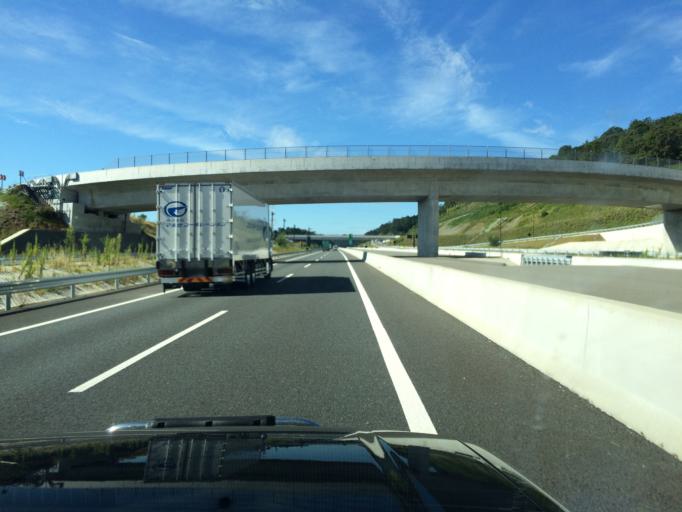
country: JP
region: Osaka
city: Ibaraki
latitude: 34.8849
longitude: 135.5353
